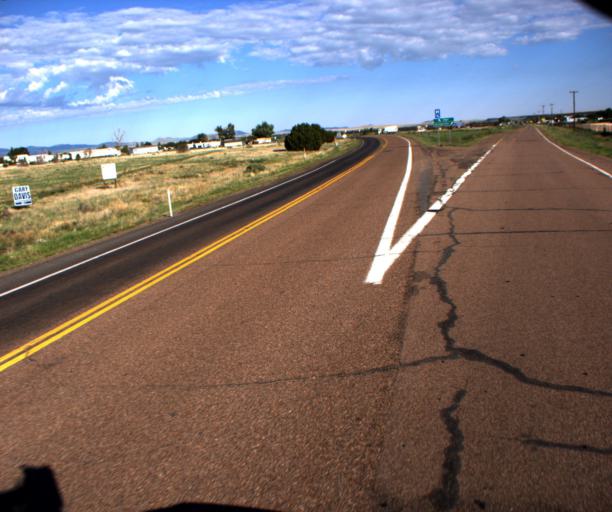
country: US
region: Arizona
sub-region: Apache County
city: Eagar
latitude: 34.1083
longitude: -109.2489
